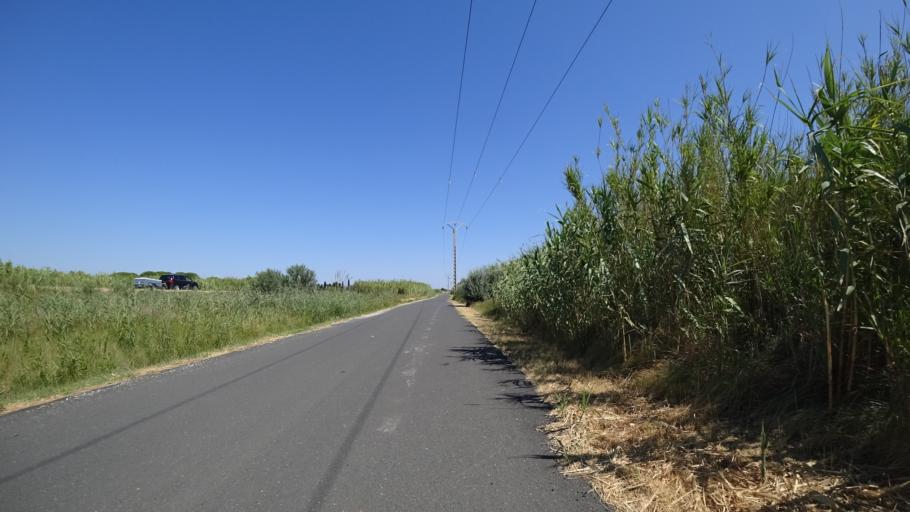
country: FR
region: Languedoc-Roussillon
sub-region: Departement des Pyrenees-Orientales
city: Le Barcares
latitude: 42.7668
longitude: 3.0186
